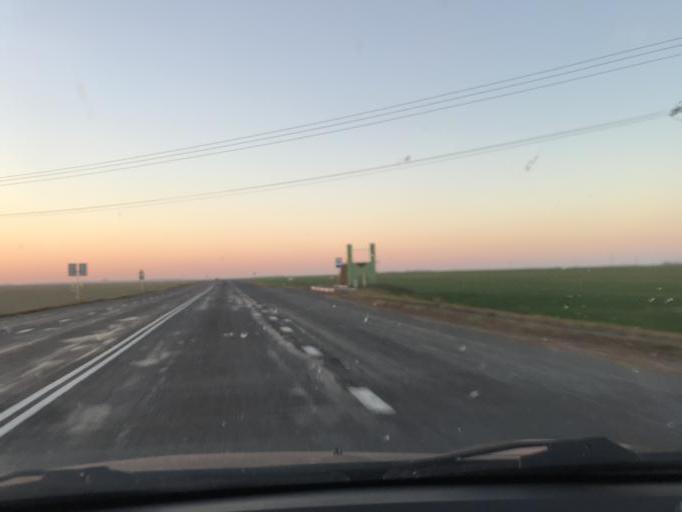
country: BY
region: Gomel
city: Loyew
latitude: 52.1515
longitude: 30.5997
